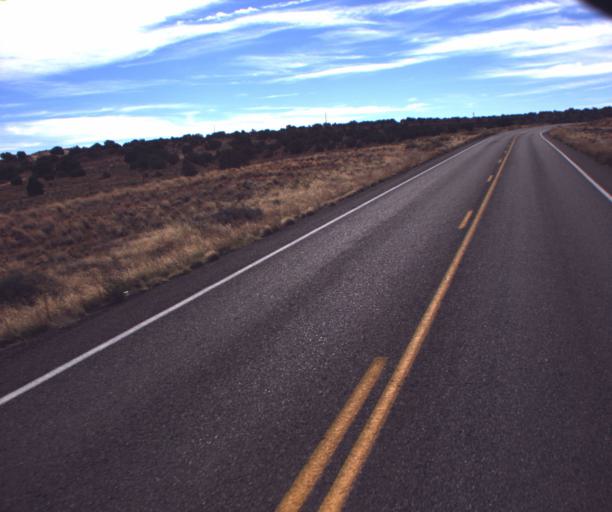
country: US
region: Arizona
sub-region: Coconino County
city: Kaibito
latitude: 36.6839
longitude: -111.2556
